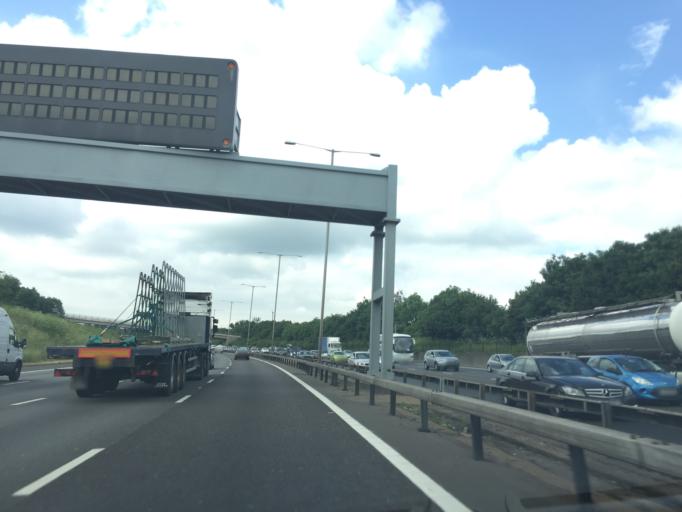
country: GB
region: England
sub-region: Greater London
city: Uxbridge
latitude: 51.5414
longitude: -0.5031
